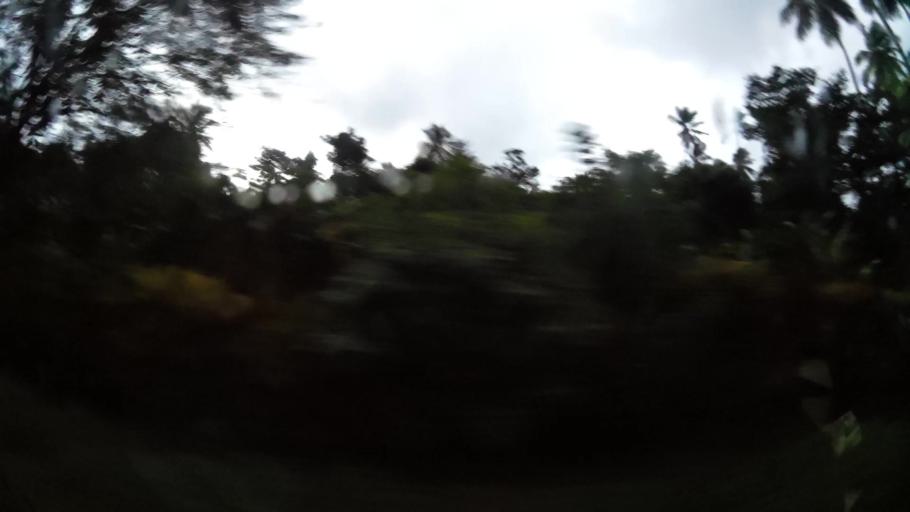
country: DM
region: Saint Andrew
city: Wesley
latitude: 15.5790
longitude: -61.3090
